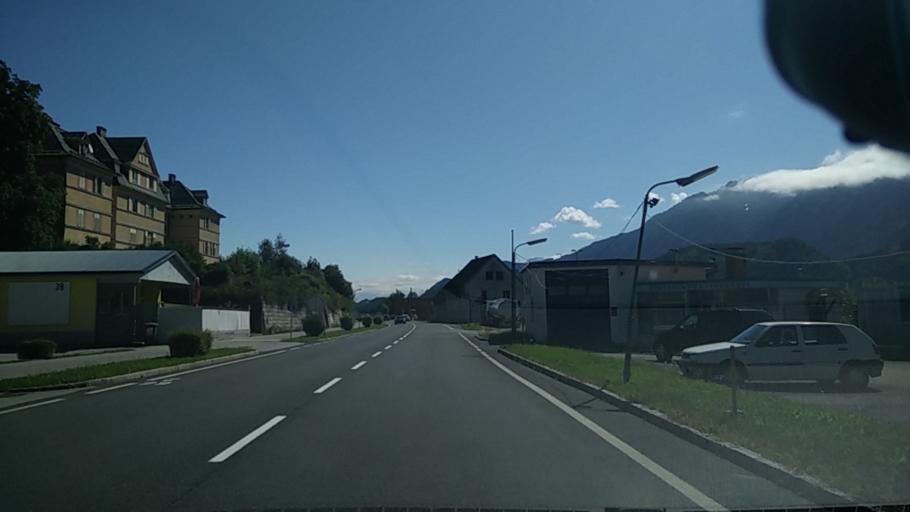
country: AT
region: Carinthia
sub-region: Politischer Bezirk Villach Land
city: Hohenthurn
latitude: 46.5420
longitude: 13.6472
